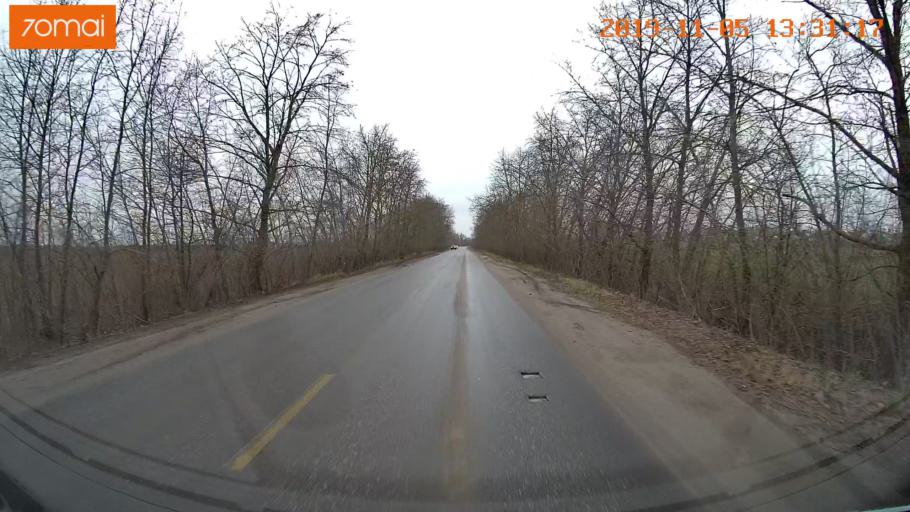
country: RU
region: Ivanovo
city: Shuya
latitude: 56.8740
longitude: 41.3927
